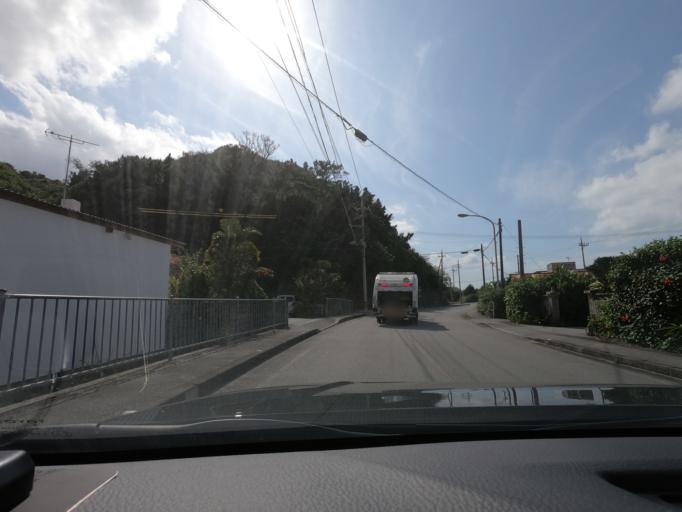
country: JP
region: Okinawa
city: Nago
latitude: 26.7559
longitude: 128.1890
